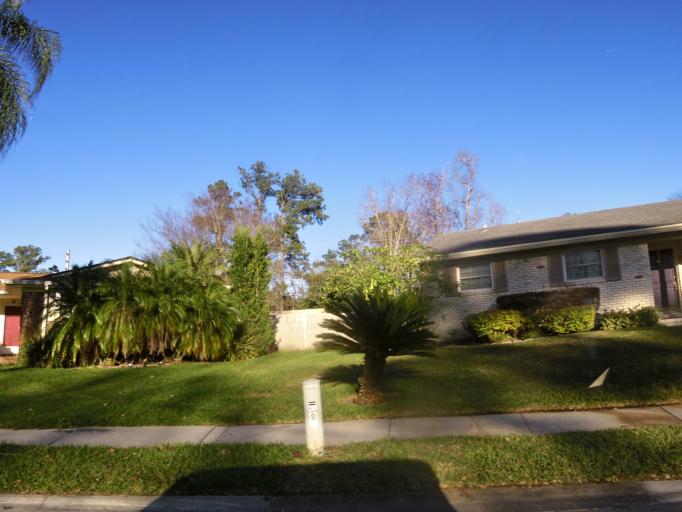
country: US
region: Florida
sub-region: Duval County
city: Jacksonville
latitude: 30.2291
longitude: -81.5973
